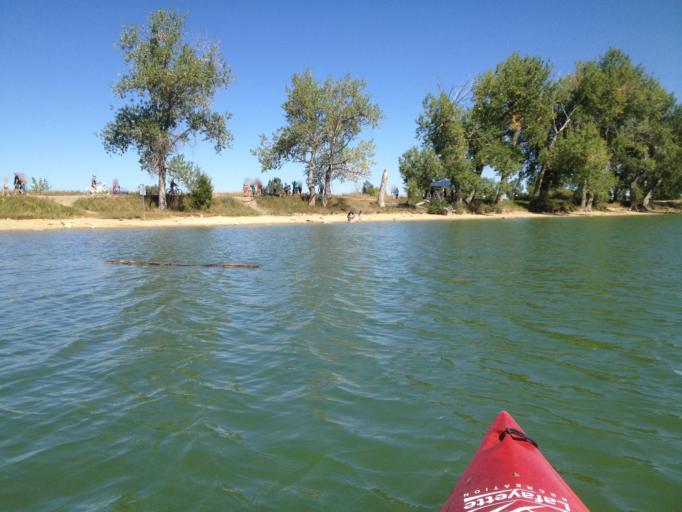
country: US
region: Colorado
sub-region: Boulder County
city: Lafayette
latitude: 39.9968
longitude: -105.1119
